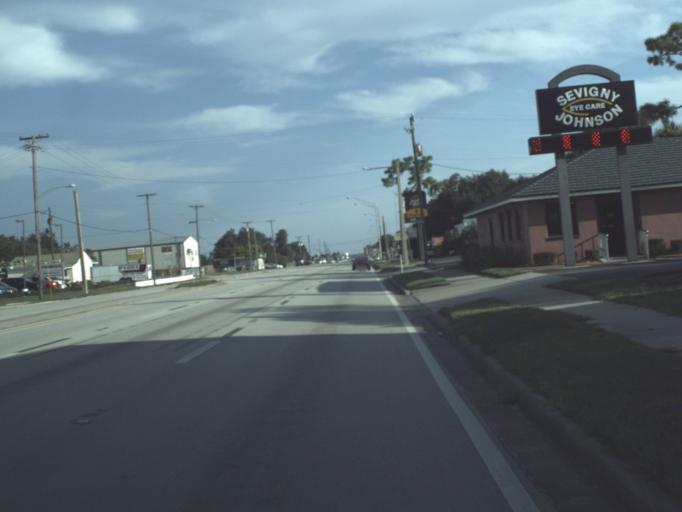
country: US
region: Florida
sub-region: Highlands County
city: Avon Park
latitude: 27.5977
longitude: -81.5143
